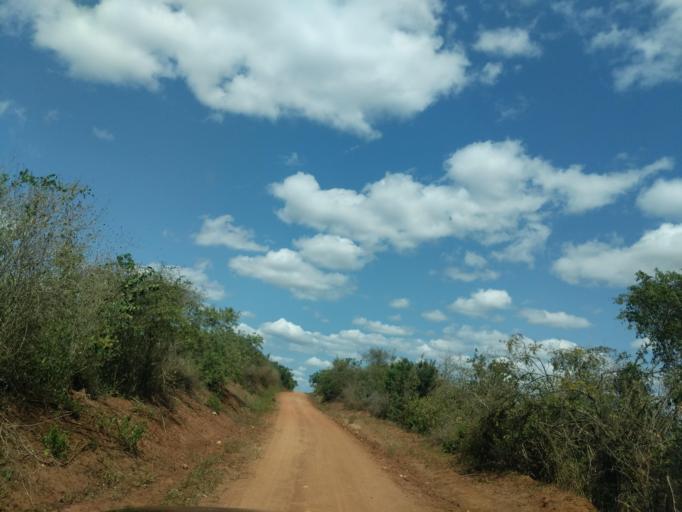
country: TZ
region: Tanga
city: Chanika
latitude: -5.5109
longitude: 38.3649
